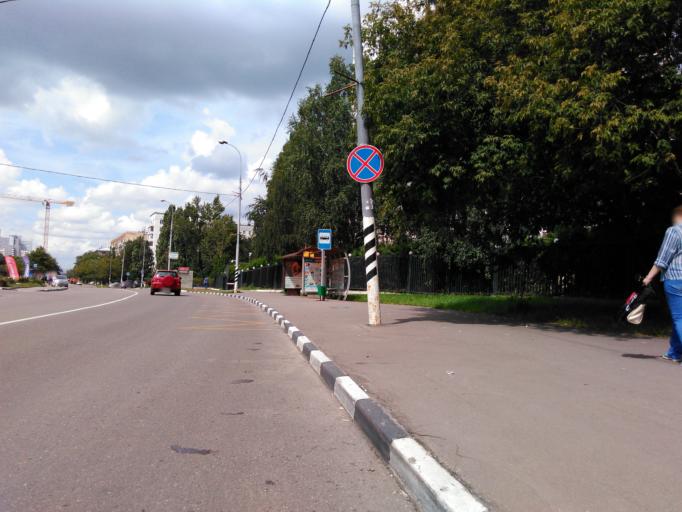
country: RU
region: Moskovskaya
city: Semenovskoye
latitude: 55.6710
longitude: 37.5298
